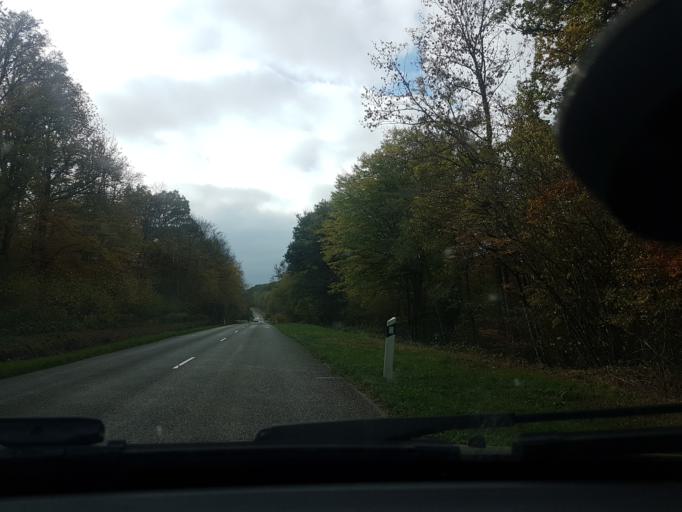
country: FR
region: Franche-Comte
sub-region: Territoire de Belfort
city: Essert
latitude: 47.6444
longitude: 6.8060
